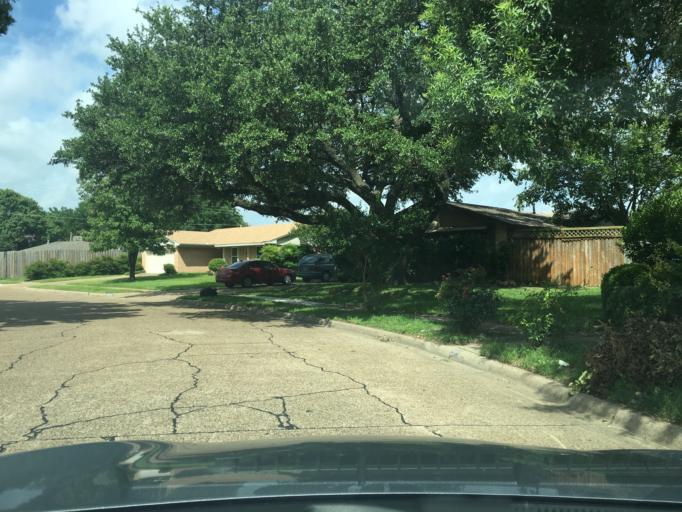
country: US
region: Texas
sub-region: Dallas County
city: Richardson
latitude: 32.9235
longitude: -96.6937
